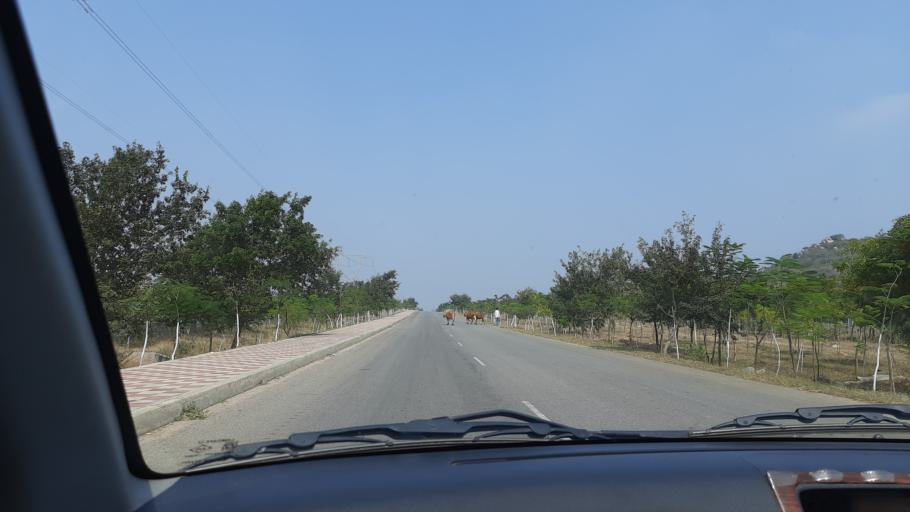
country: IN
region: Telangana
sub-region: Rangareddi
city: Lal Bahadur Nagar
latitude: 17.2871
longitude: 78.6506
